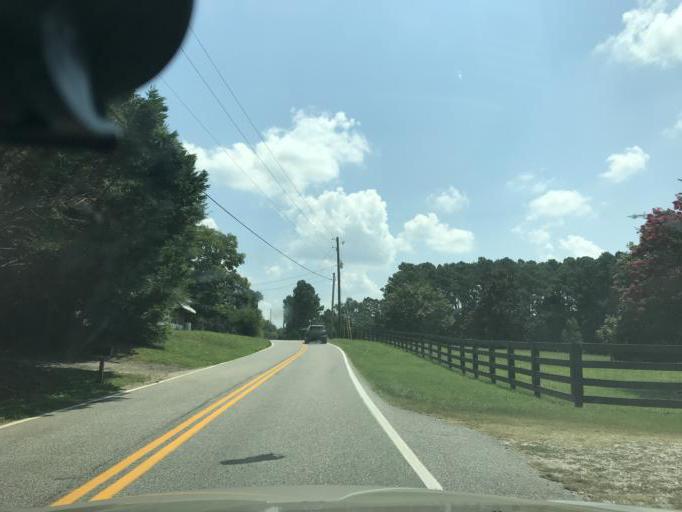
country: US
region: Georgia
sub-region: Dawson County
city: Dawsonville
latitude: 34.3169
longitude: -84.1472
